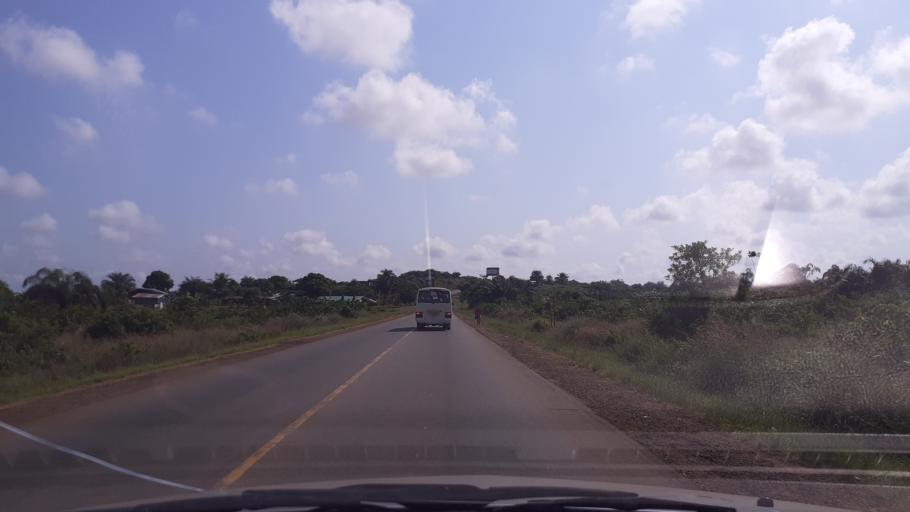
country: LR
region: Montserrado
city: Bensonville City
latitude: 6.2095
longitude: -10.5613
